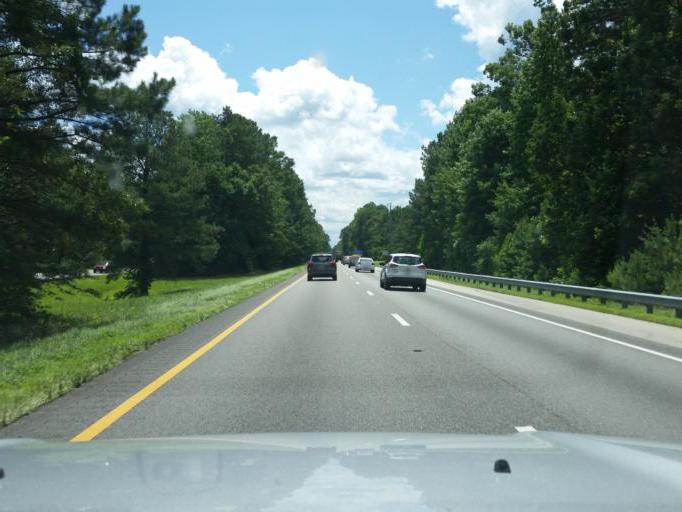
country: US
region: Virginia
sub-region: City of Williamsburg
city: Williamsburg
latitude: 37.3413
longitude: -76.7189
